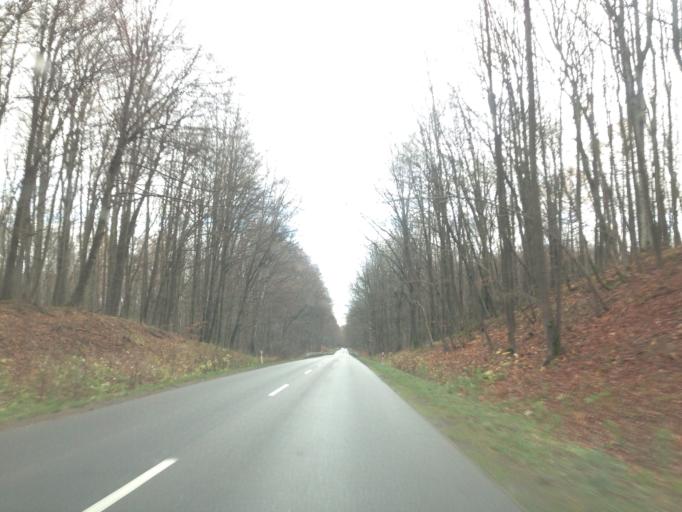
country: PL
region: Pomeranian Voivodeship
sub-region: Powiat gdanski
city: Kolbudy
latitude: 54.2535
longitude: 18.4078
